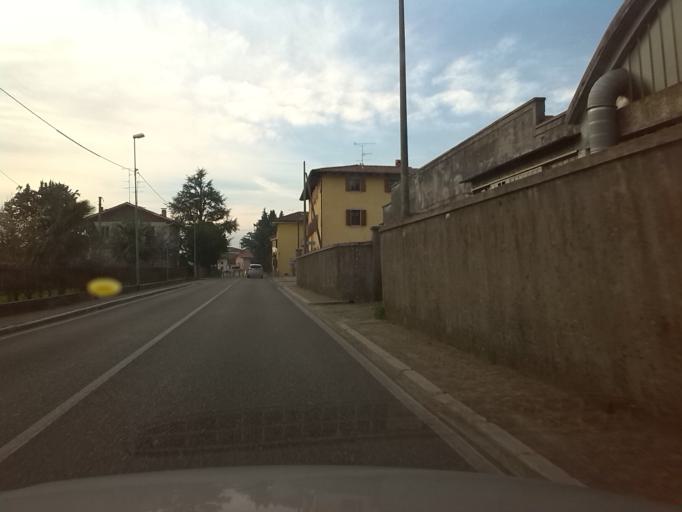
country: IT
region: Friuli Venezia Giulia
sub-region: Provincia di Udine
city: Corno di Rosazzo
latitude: 45.9995
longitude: 13.4403
